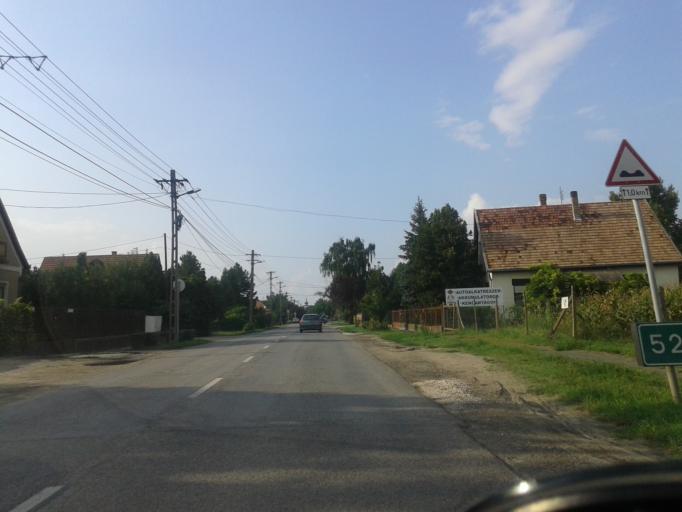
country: HU
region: Pest
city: Domsod
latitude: 47.0825
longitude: 19.0059
